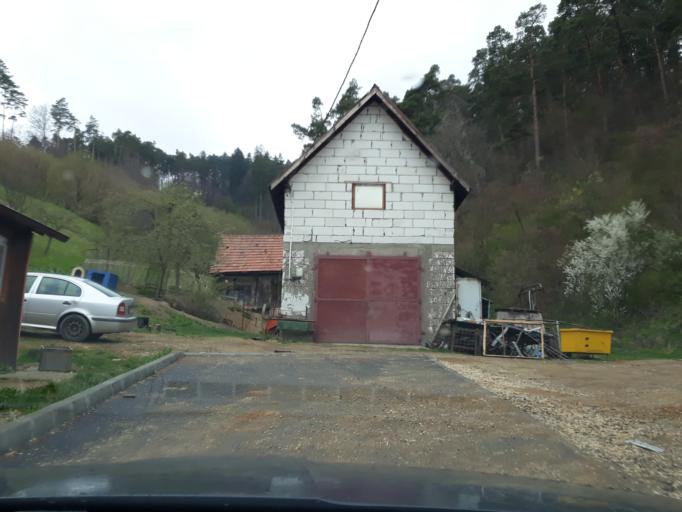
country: RO
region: Brasov
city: Codlea
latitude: 45.7010
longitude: 25.4321
